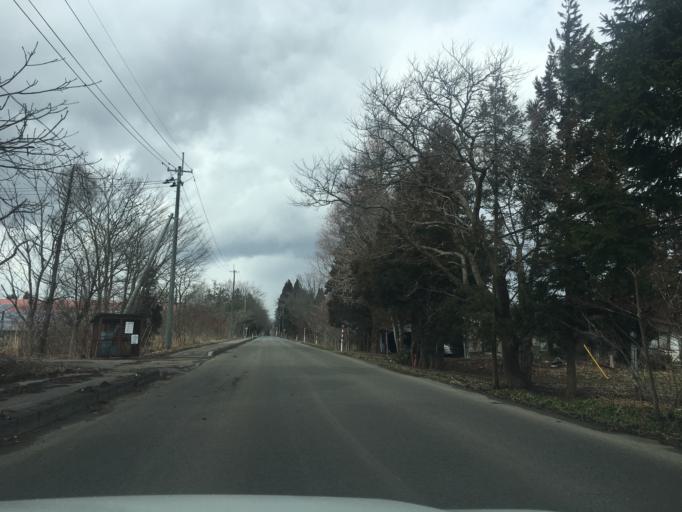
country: JP
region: Akita
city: Takanosu
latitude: 40.1792
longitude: 140.3461
